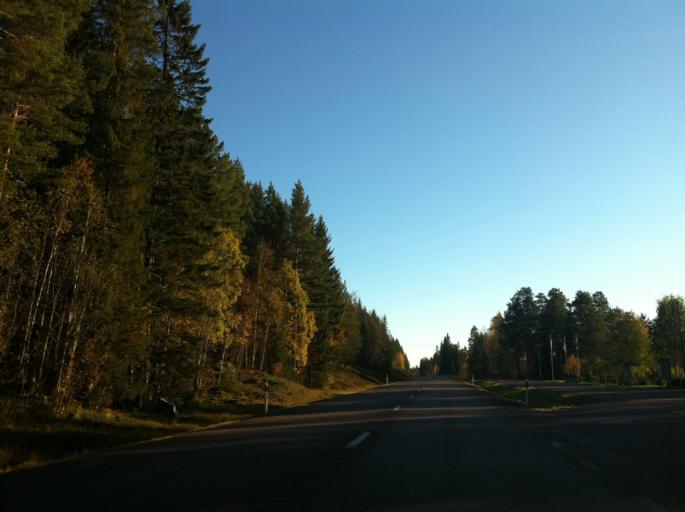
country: SE
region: Dalarna
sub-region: Faluns Kommun
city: Bjursas
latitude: 60.7754
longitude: 15.3166
